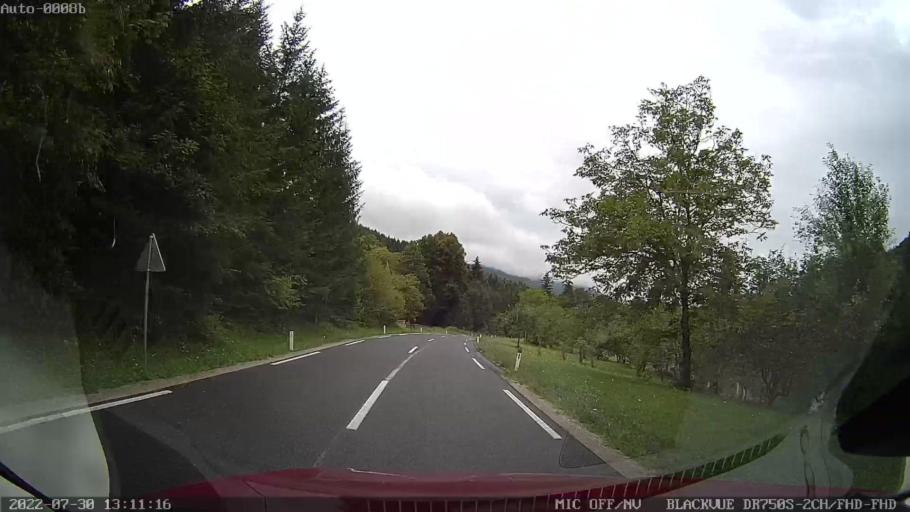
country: SI
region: Dolenjske Toplice
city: Dolenjske Toplice
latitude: 45.7019
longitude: 15.0799
